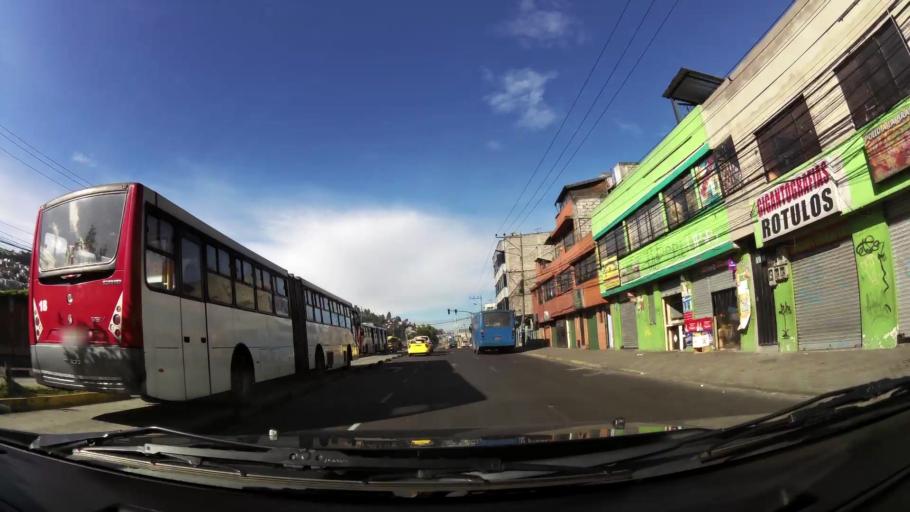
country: EC
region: Pichincha
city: Quito
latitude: -0.2724
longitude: -78.5293
